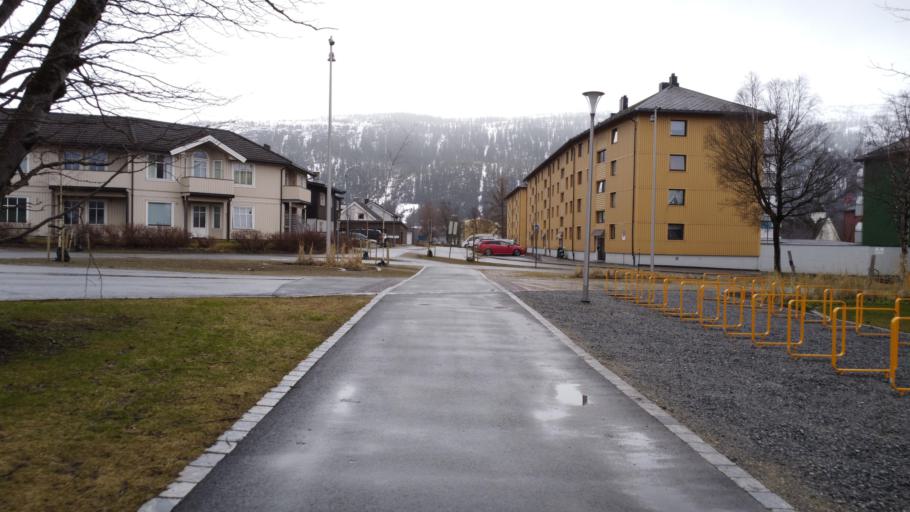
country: NO
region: Nordland
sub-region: Rana
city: Mo i Rana
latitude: 66.3118
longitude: 14.1454
